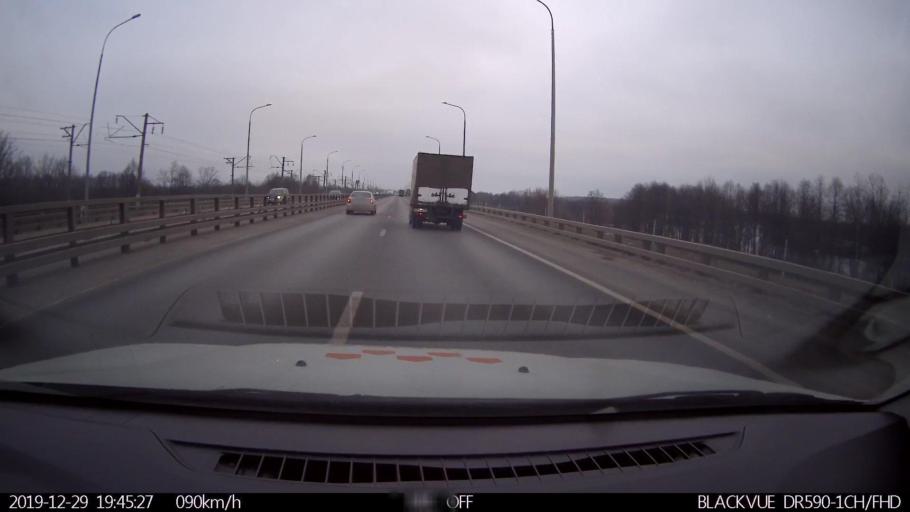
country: RU
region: Nizjnij Novgorod
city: Neklyudovo
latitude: 56.3868
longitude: 43.9682
